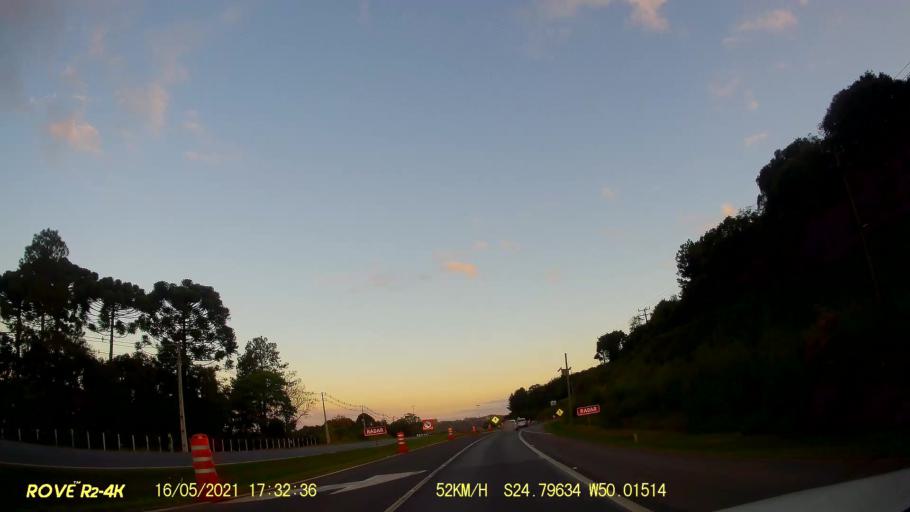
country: BR
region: Parana
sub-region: Castro
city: Castro
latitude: -24.7965
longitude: -50.0151
